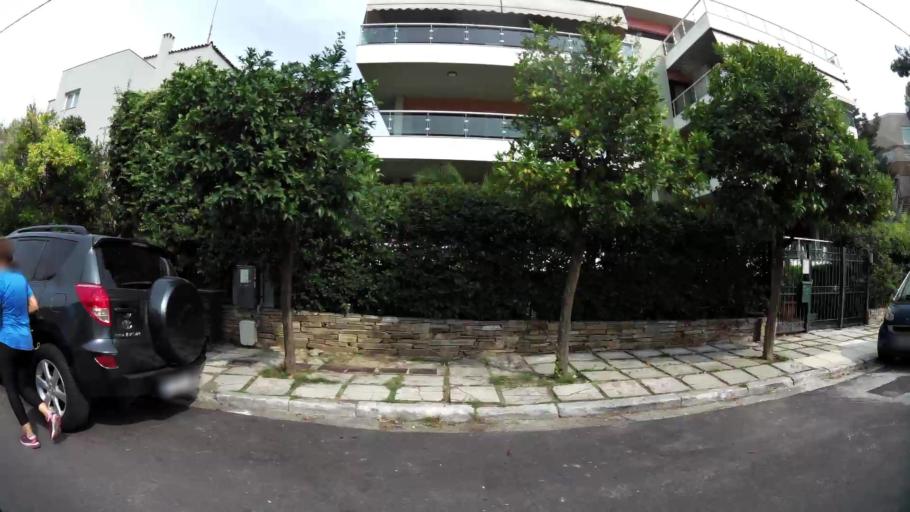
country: GR
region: Attica
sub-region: Nomarchia Athinas
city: Filothei
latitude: 38.0231
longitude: 23.7824
